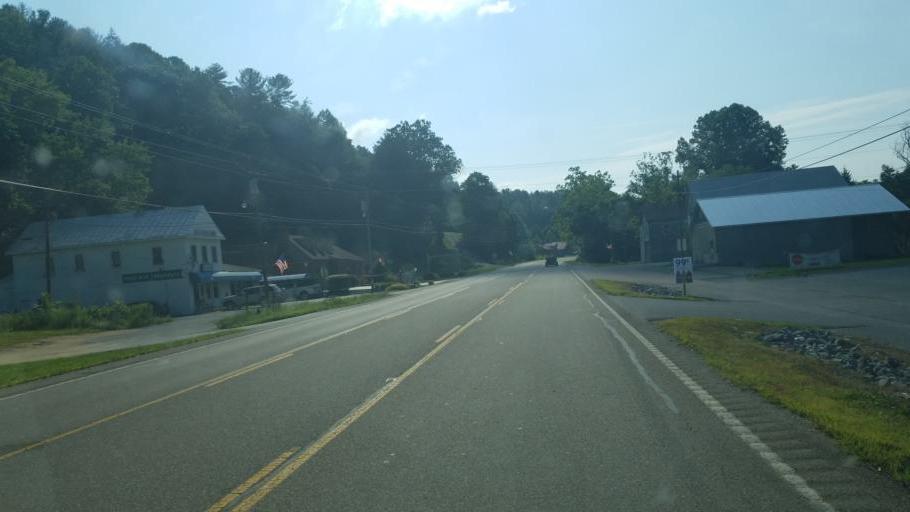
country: US
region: Tennessee
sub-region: Carter County
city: Roan Mountain
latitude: 36.1994
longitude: -82.0712
